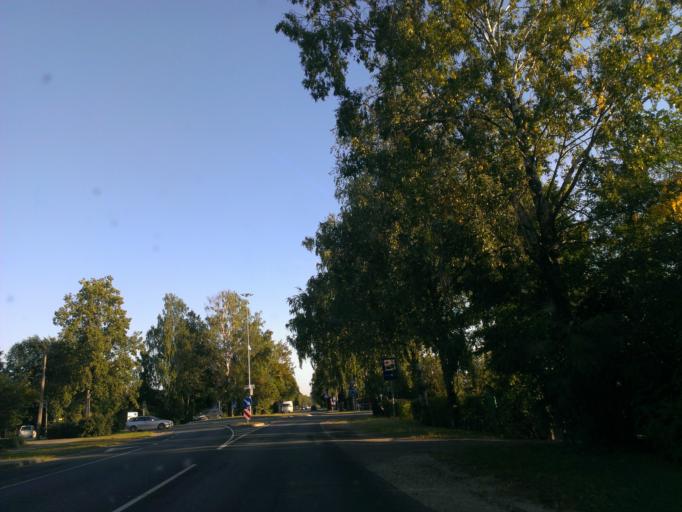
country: LV
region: Adazi
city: Adazi
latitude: 57.0765
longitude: 24.3195
